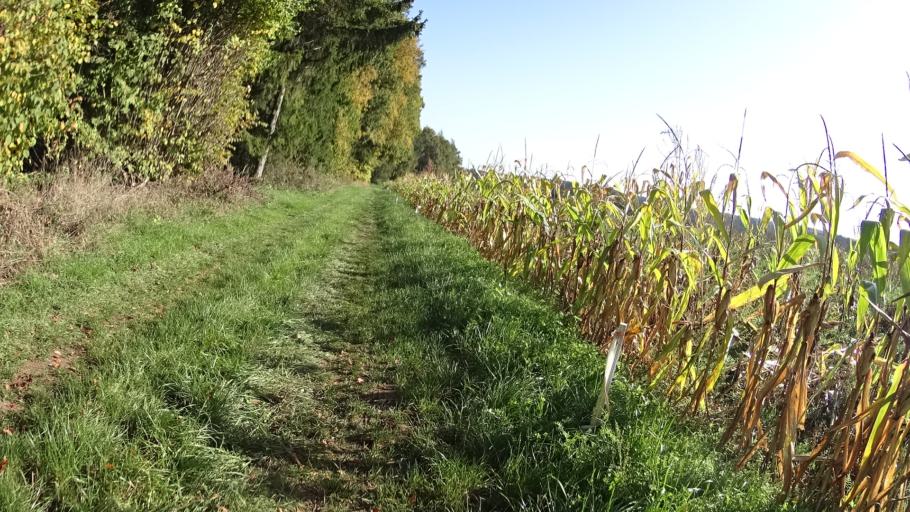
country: DE
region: Bavaria
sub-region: Upper Bavaria
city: Bohmfeld
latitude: 48.8733
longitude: 11.3557
